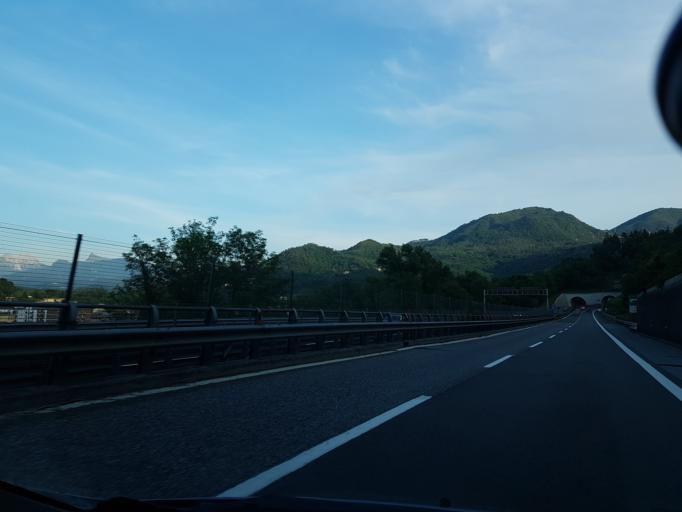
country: IT
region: Tuscany
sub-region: Provincia di Massa-Carrara
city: Aulla
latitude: 44.2121
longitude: 9.9629
